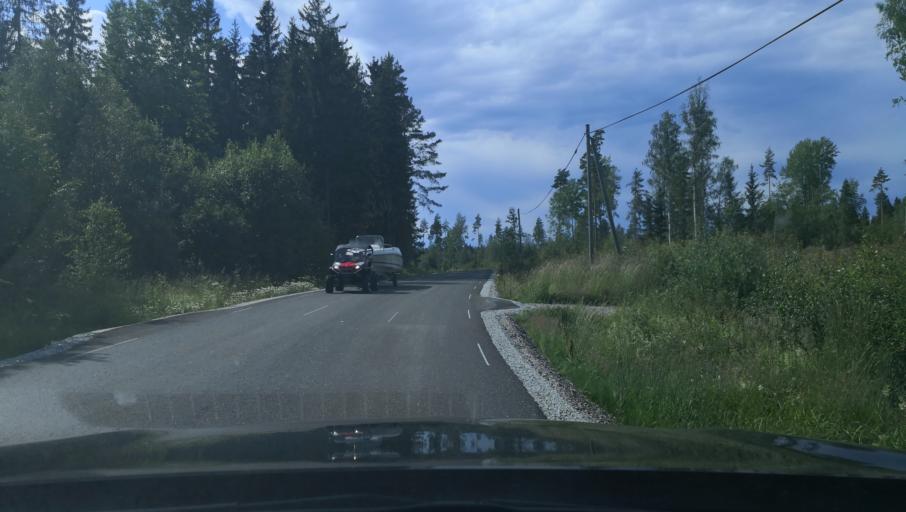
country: SE
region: Vaestmanland
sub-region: Norbergs Kommun
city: Norberg
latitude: 59.9673
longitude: 15.9785
